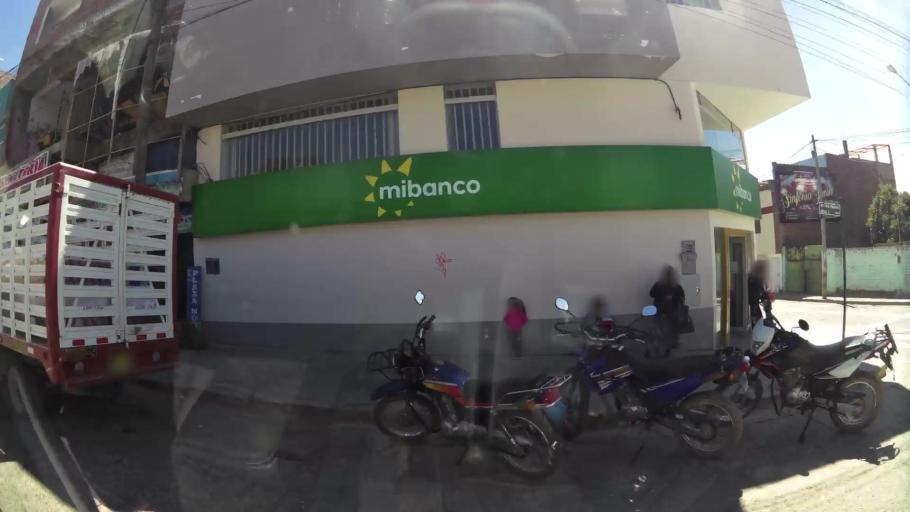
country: PE
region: Junin
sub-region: Provincia de Jauja
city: Jauja
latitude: -11.7782
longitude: -75.4976
